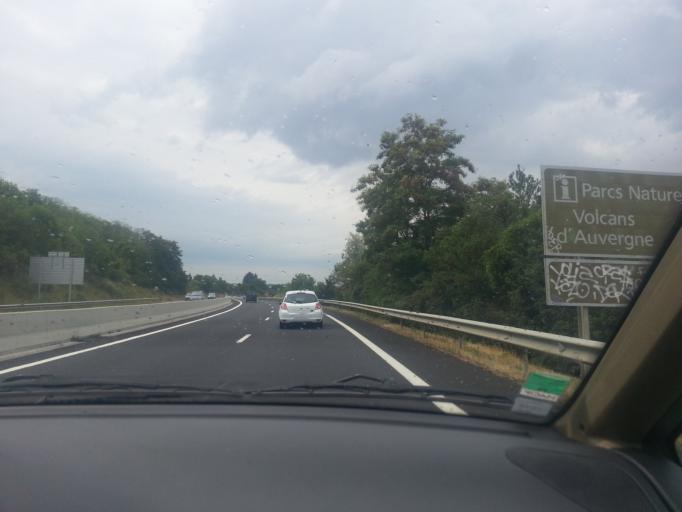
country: FR
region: Auvergne
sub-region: Departement du Puy-de-Dome
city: Issoire
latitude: 45.5186
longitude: 3.2600
